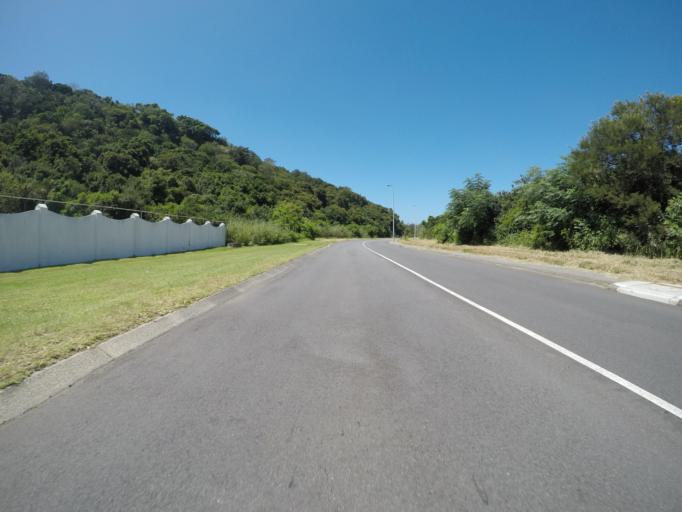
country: ZA
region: Eastern Cape
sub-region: Buffalo City Metropolitan Municipality
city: East London
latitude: -32.9752
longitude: 27.9333
